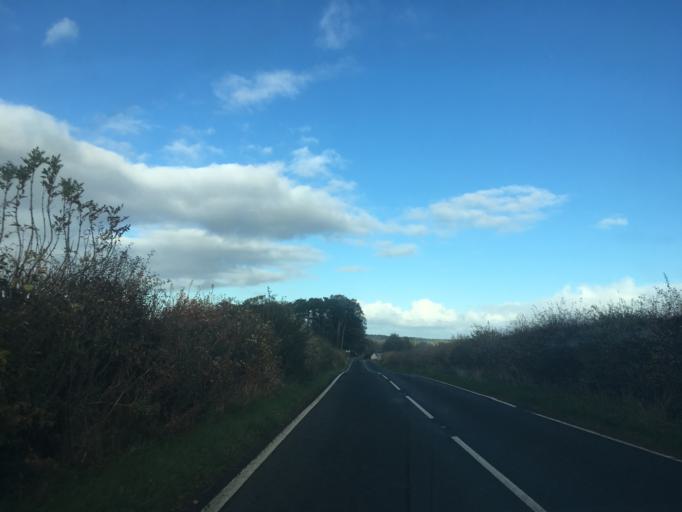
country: GB
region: Scotland
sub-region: East Lothian
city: Pencaitland
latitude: 55.8507
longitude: -2.8727
